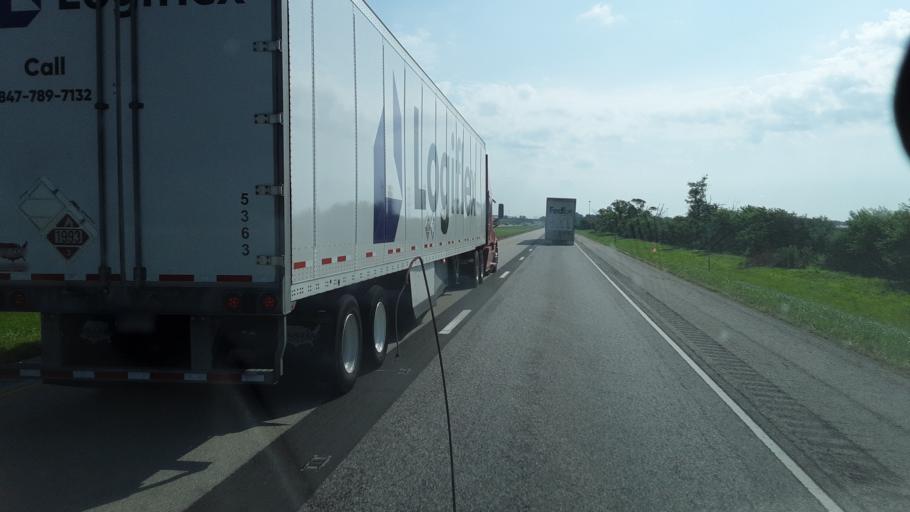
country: US
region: Illinois
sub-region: Fayette County
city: Vandalia
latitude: 38.9654
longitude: -89.1439
